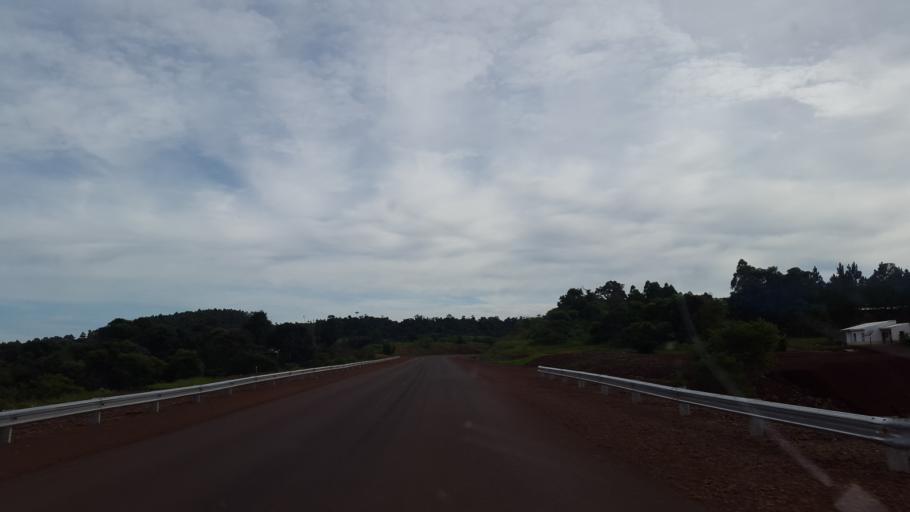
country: AR
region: Misiones
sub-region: Departamento de San Pedro
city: San Pedro
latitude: -26.4593
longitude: -53.8730
